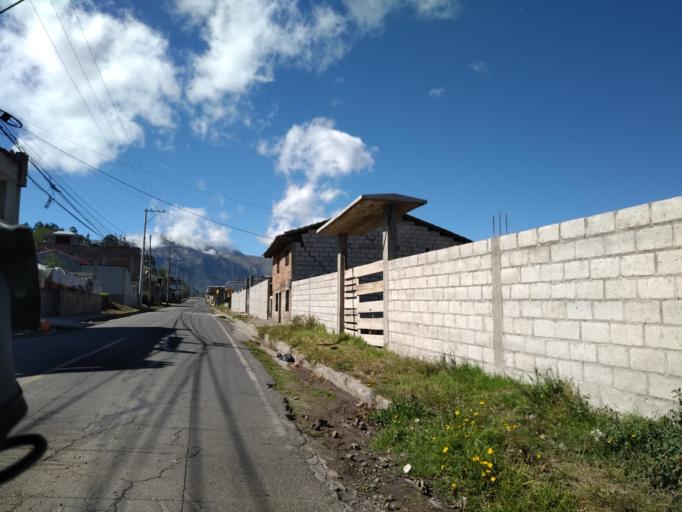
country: EC
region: Imbabura
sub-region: Canton Otavalo
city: Otavalo
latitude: 0.2148
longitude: -78.2136
